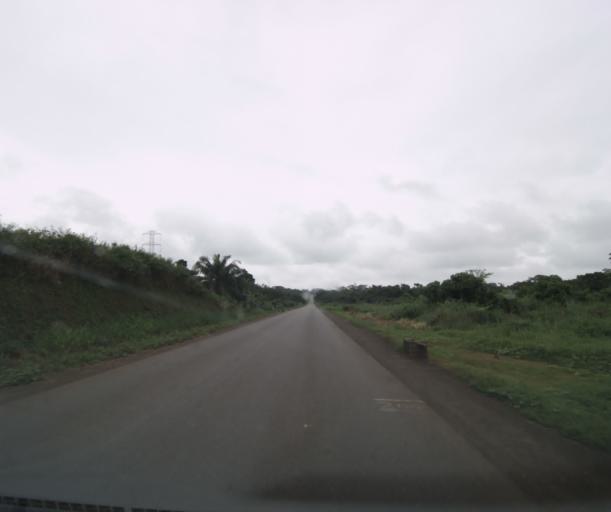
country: CM
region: Littoral
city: Edea
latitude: 3.7094
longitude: 10.1080
